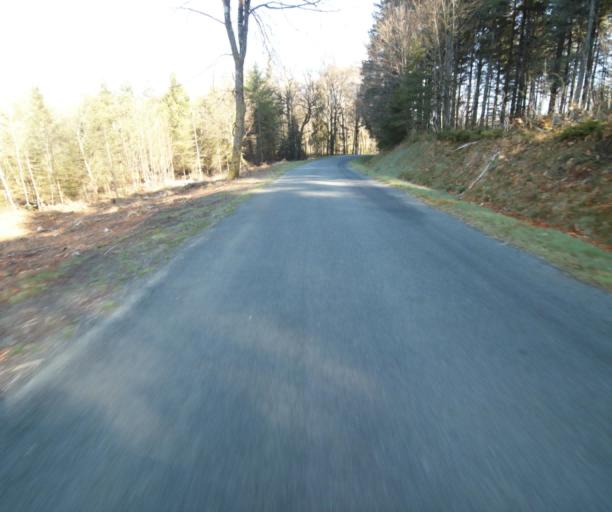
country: FR
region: Limousin
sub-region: Departement de la Correze
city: Correze
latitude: 45.2924
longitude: 1.8692
